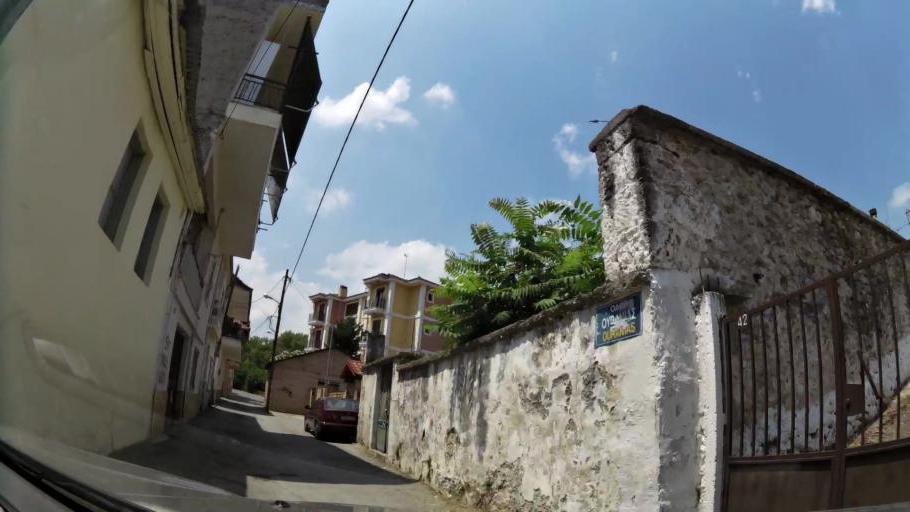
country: GR
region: Central Macedonia
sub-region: Nomos Imathias
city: Veroia
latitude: 40.5209
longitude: 22.1962
